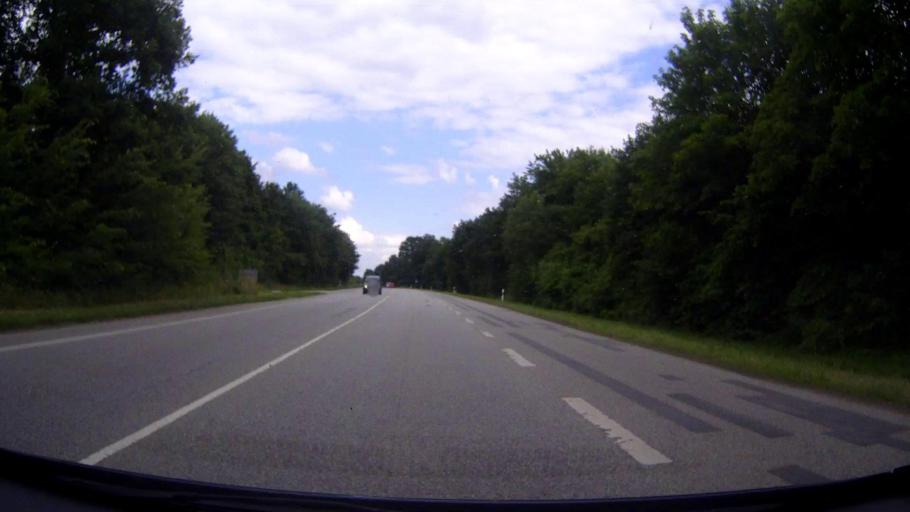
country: DE
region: Schleswig-Holstein
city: Stockelsdorf
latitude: 53.8920
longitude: 10.6079
